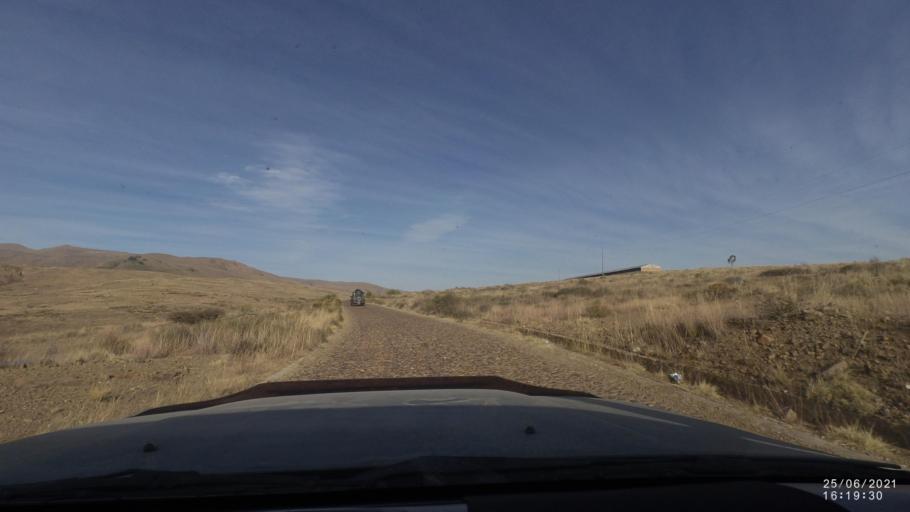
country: BO
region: Cochabamba
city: Cliza
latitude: -17.7409
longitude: -65.8461
